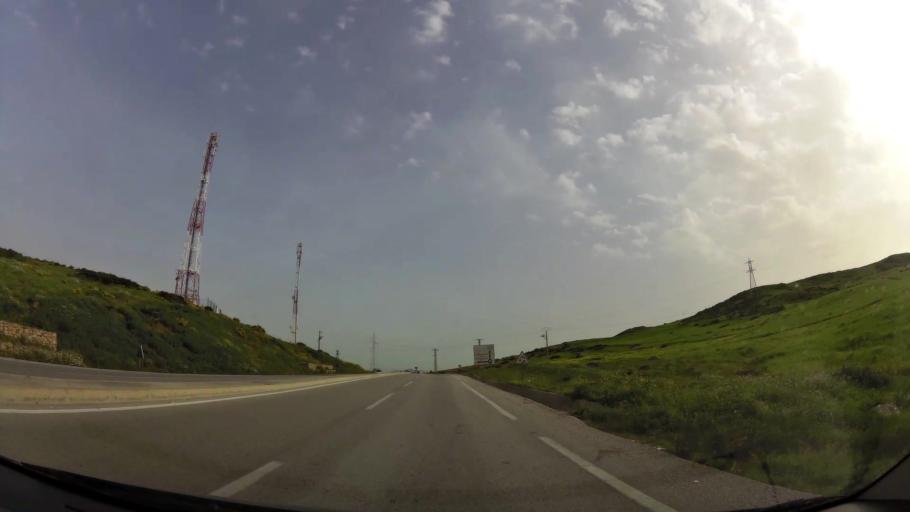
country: MA
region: Tanger-Tetouan
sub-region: Tanger-Assilah
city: Dar Chaoui
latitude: 35.6386
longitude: -5.6840
